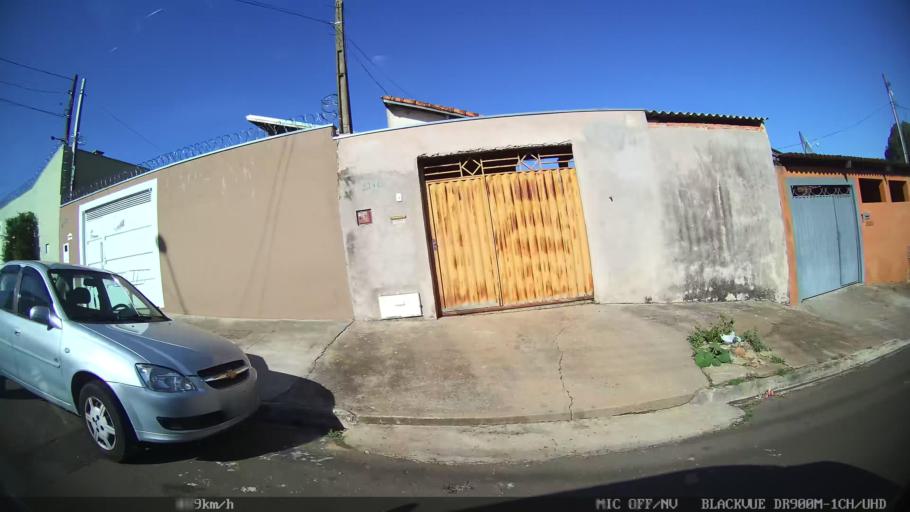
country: BR
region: Sao Paulo
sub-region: Franca
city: Franca
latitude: -20.4921
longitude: -47.4134
